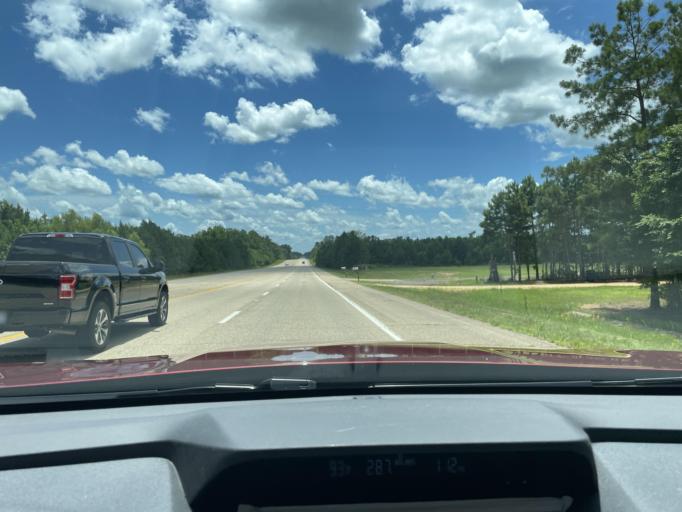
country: US
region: Arkansas
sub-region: Drew County
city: Monticello
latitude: 33.6856
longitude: -91.8057
